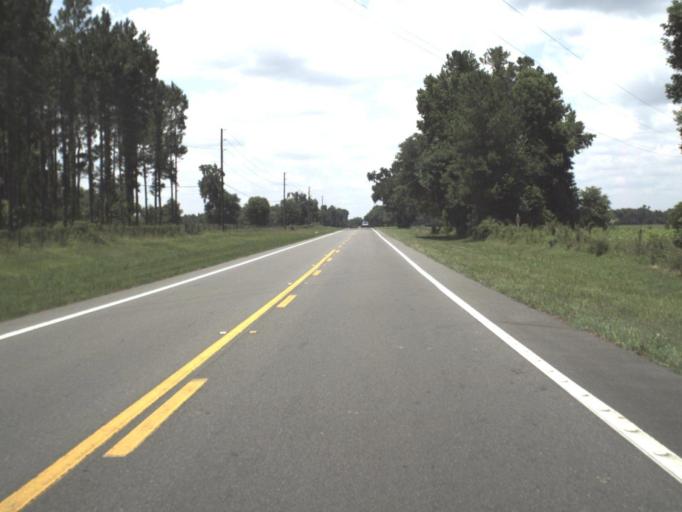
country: US
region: Florida
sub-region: Alachua County
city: Archer
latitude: 29.5055
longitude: -82.4065
